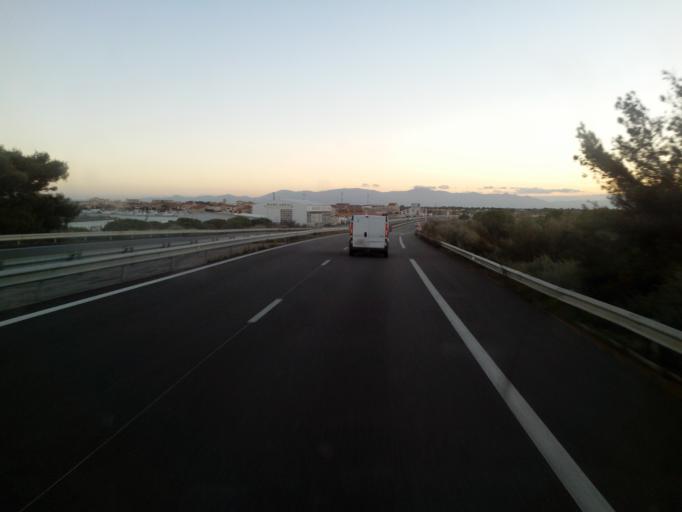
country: FR
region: Languedoc-Roussillon
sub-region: Departement des Pyrenees-Orientales
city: Le Barcares
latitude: 42.8049
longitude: 3.0308
